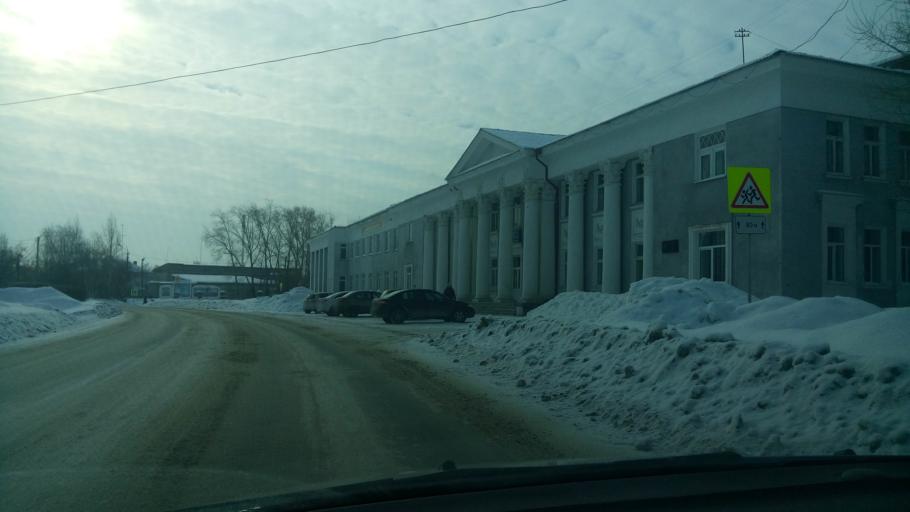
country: RU
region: Sverdlovsk
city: Bogdanovich
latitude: 56.7739
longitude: 62.0553
